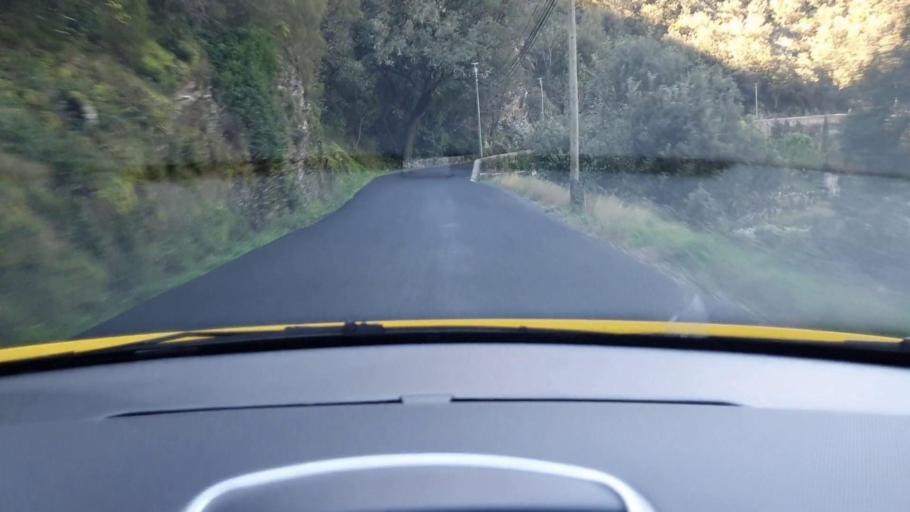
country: FR
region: Languedoc-Roussillon
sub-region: Departement du Gard
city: Sumene
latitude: 43.9927
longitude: 3.7121
